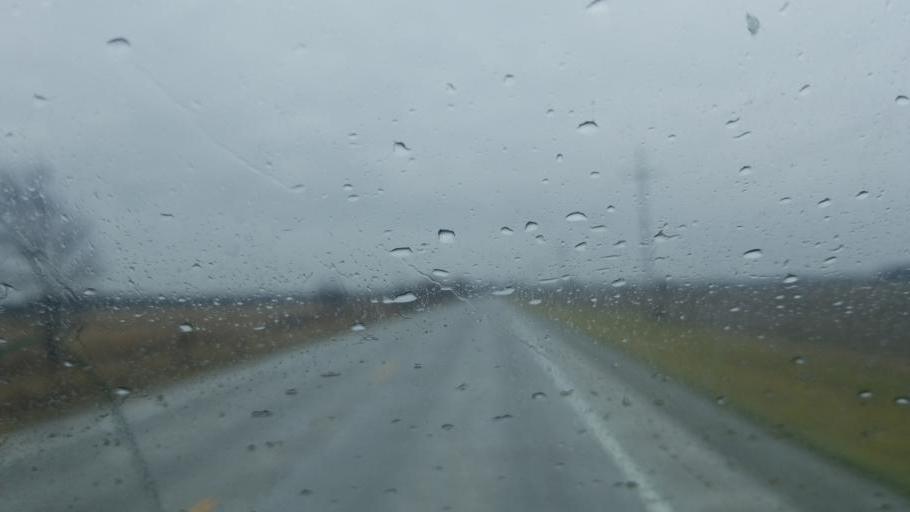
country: US
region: Indiana
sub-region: Shelby County
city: Geneva
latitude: 39.4076
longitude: -85.7508
